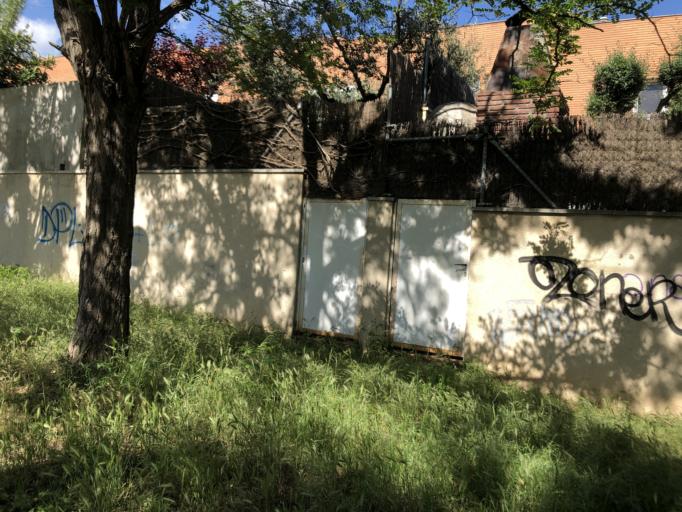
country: ES
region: Catalonia
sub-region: Provincia de Barcelona
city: Rubi
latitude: 41.4910
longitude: 2.0415
